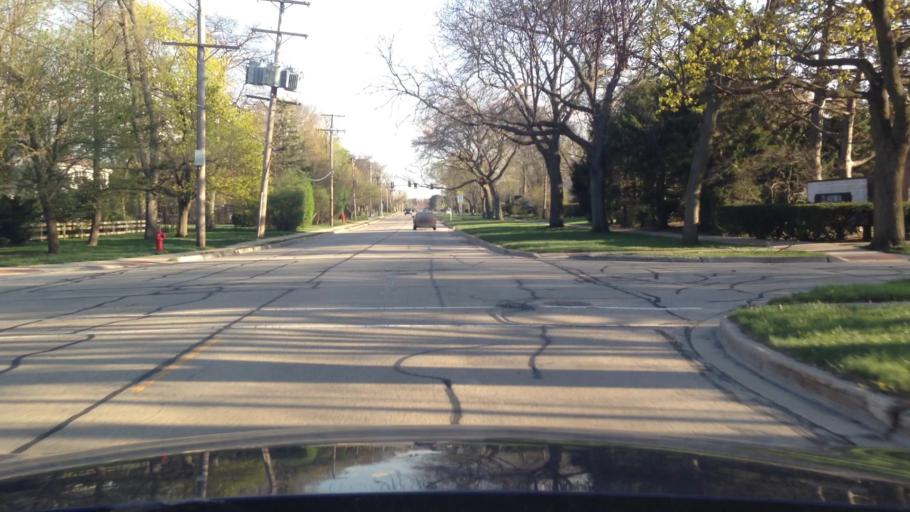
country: US
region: Illinois
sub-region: Lake County
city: Deerfield
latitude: 42.1617
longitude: -87.8673
